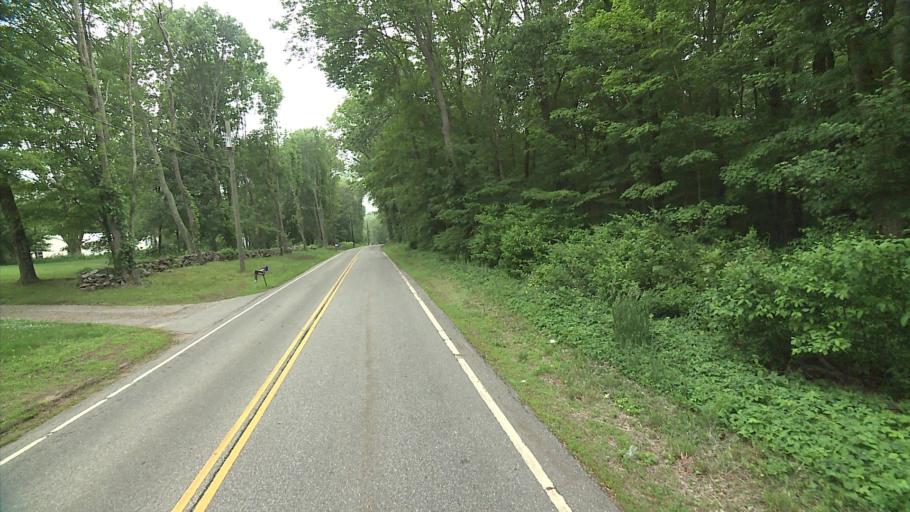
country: US
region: Connecticut
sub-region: Tolland County
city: Hebron
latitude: 41.6800
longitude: -72.3594
